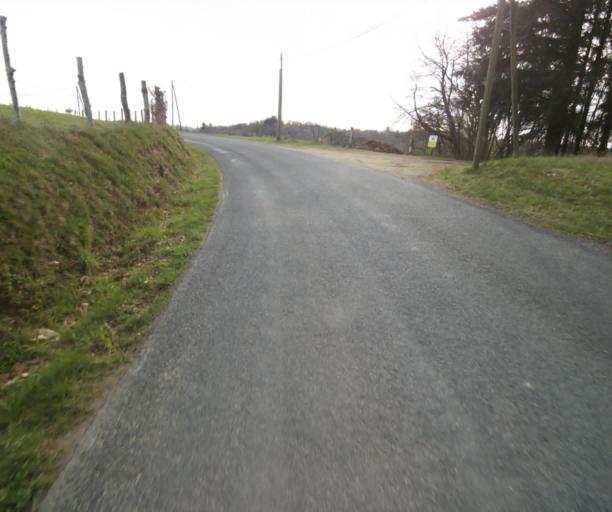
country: FR
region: Limousin
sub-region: Departement de la Correze
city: Correze
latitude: 45.3567
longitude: 1.8484
